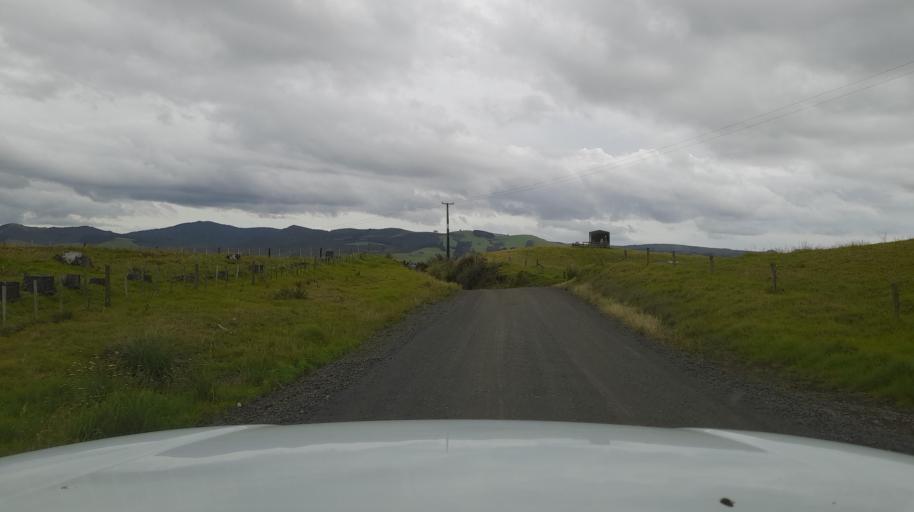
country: NZ
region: Northland
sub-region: Far North District
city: Ahipara
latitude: -35.1323
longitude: 173.1845
